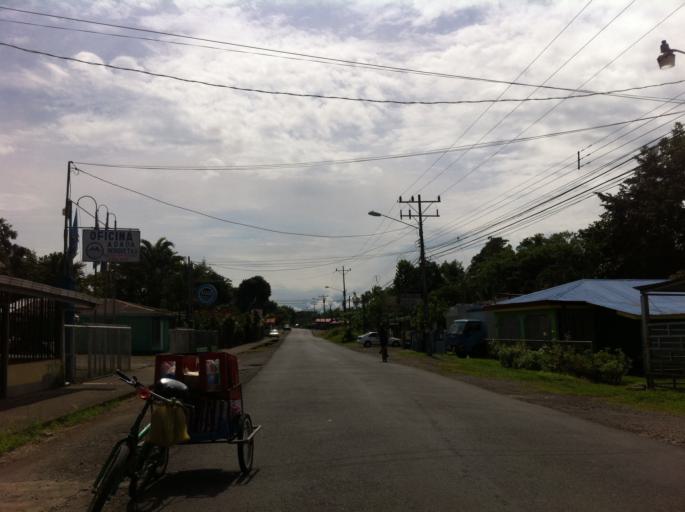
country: CR
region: Heredia
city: La Virgen
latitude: 10.3391
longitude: -83.9567
